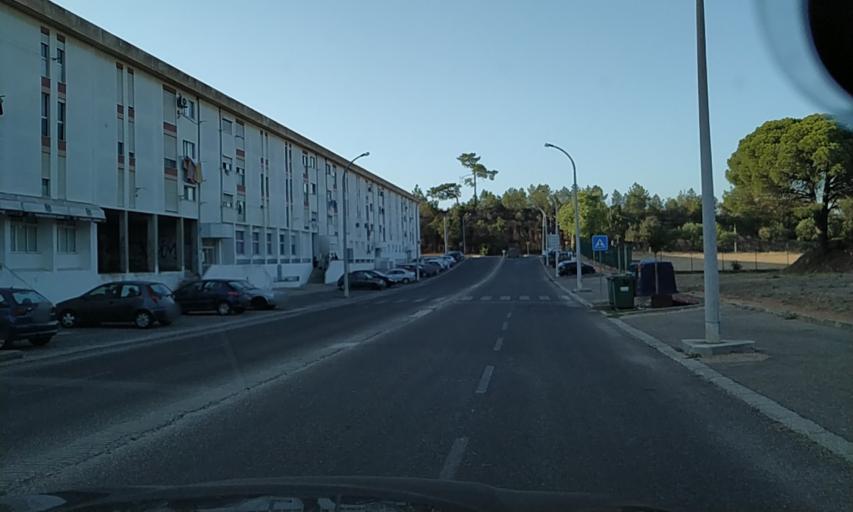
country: PT
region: Setubal
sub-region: Setubal
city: Setubal
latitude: 38.5213
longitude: -8.8598
